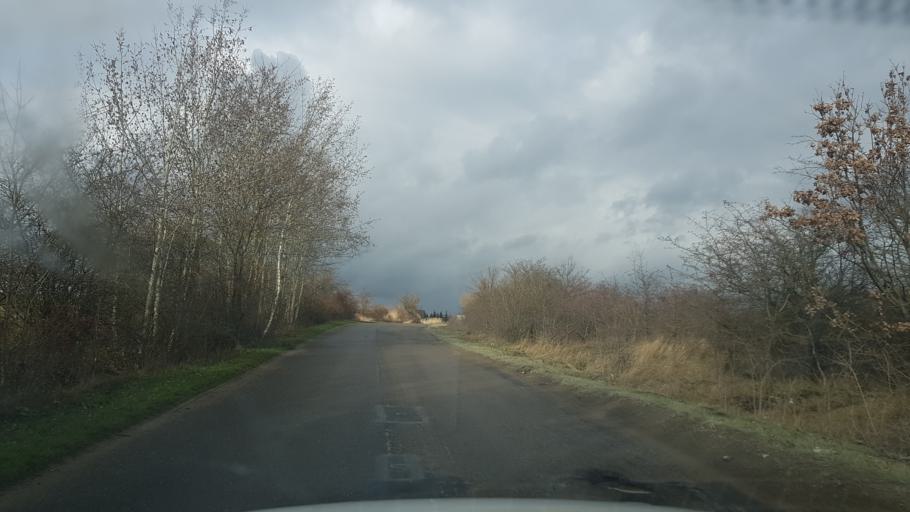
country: PL
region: West Pomeranian Voivodeship
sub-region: Powiat policki
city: Kolbaskowo
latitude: 53.3501
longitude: 14.4407
